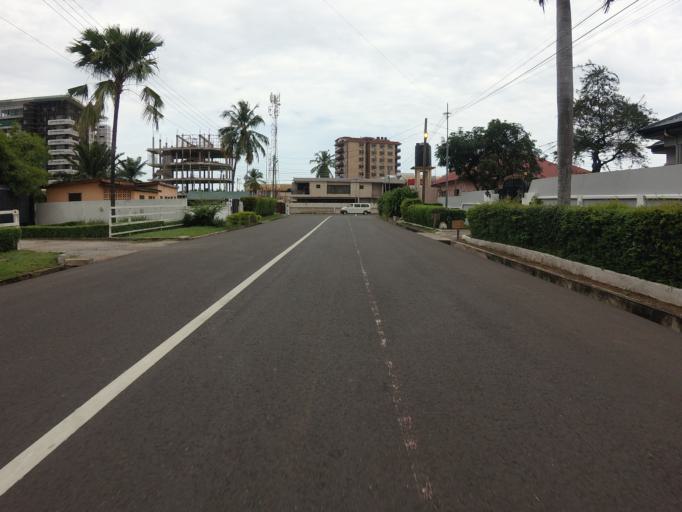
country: GH
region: Greater Accra
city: Dome
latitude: 5.6127
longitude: -0.2031
